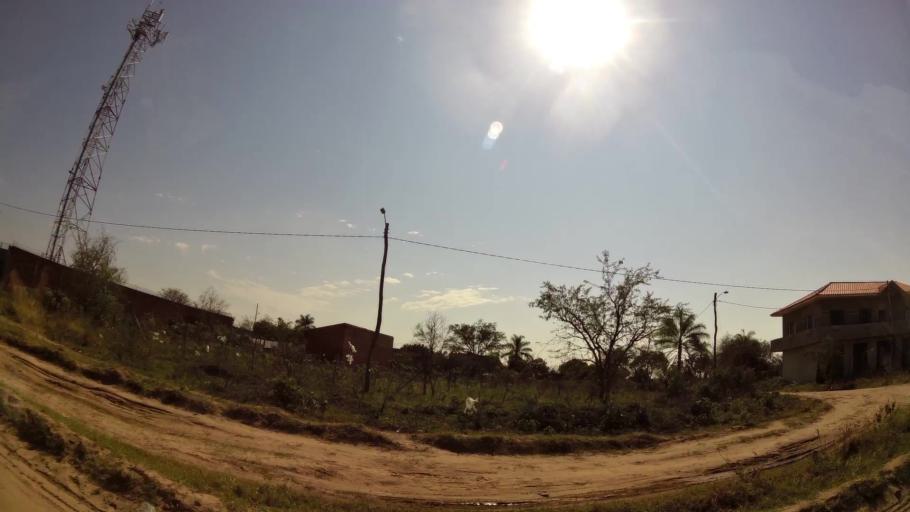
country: BO
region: Santa Cruz
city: Cotoca
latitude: -17.7276
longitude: -63.0710
